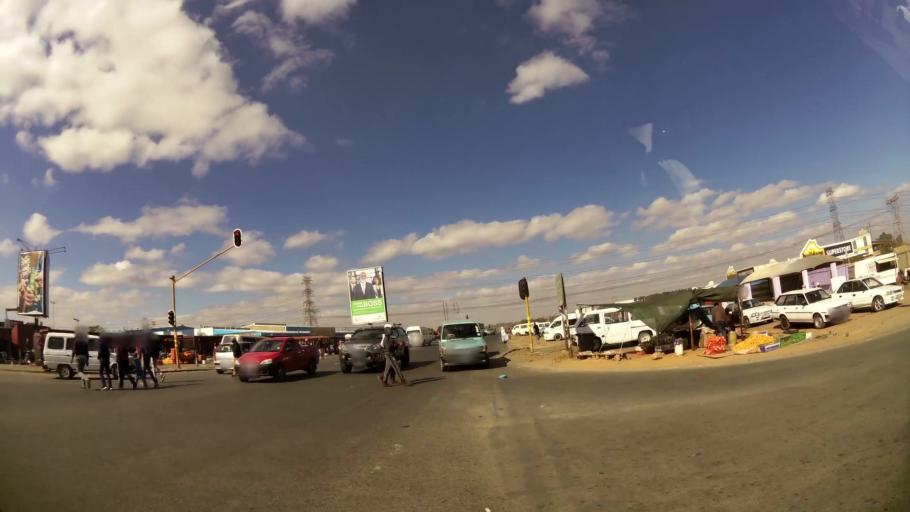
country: ZA
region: Gauteng
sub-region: City of Johannesburg Metropolitan Municipality
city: Modderfontein
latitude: -26.0334
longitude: 28.1742
